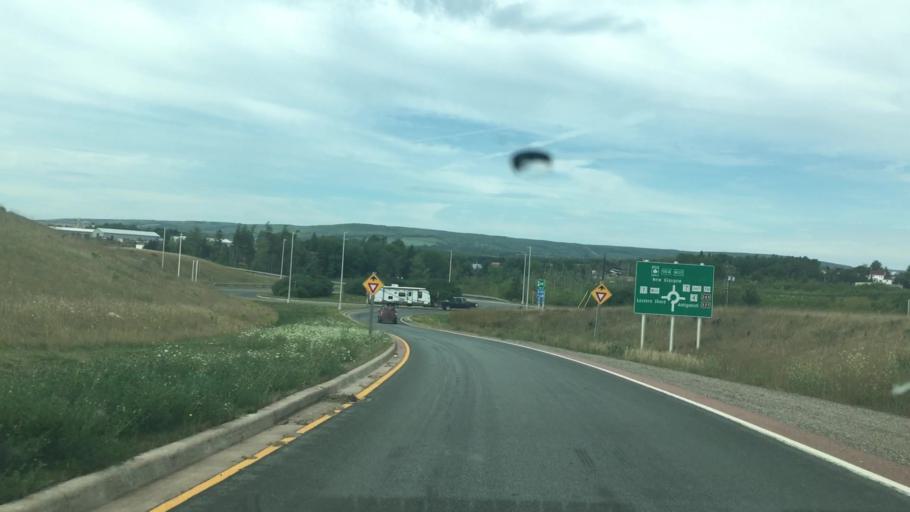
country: CA
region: Nova Scotia
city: Antigonish
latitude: 45.6120
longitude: -61.9973
